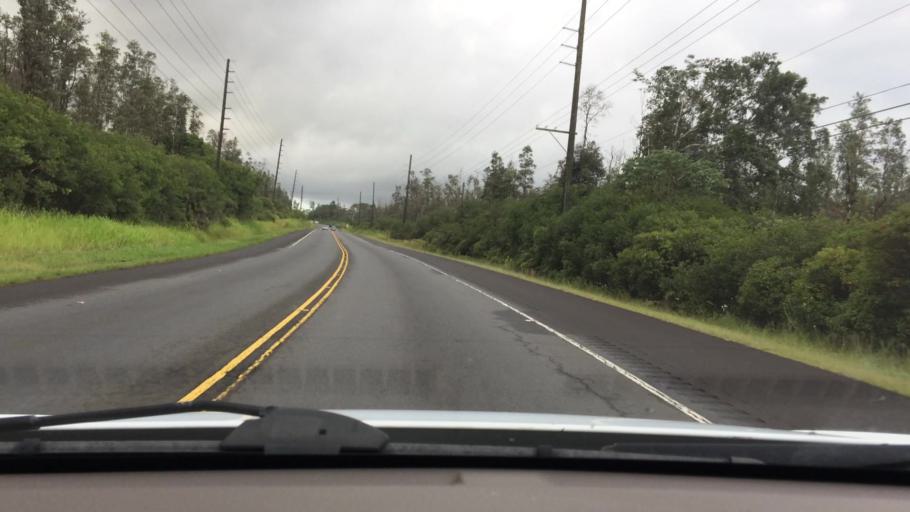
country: US
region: Hawaii
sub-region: Hawaii County
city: Ainaloa
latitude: 19.5272
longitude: -154.9706
